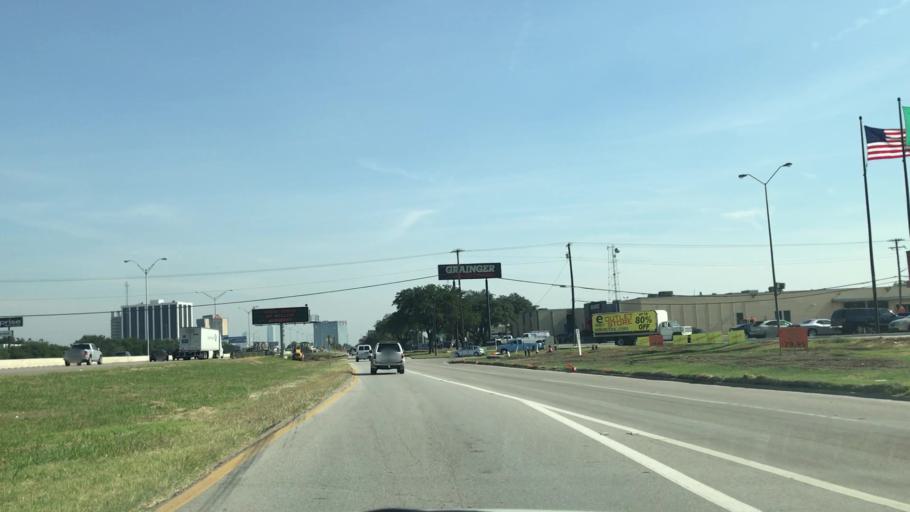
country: US
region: Texas
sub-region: Dallas County
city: Irving
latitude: 32.8226
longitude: -96.8791
